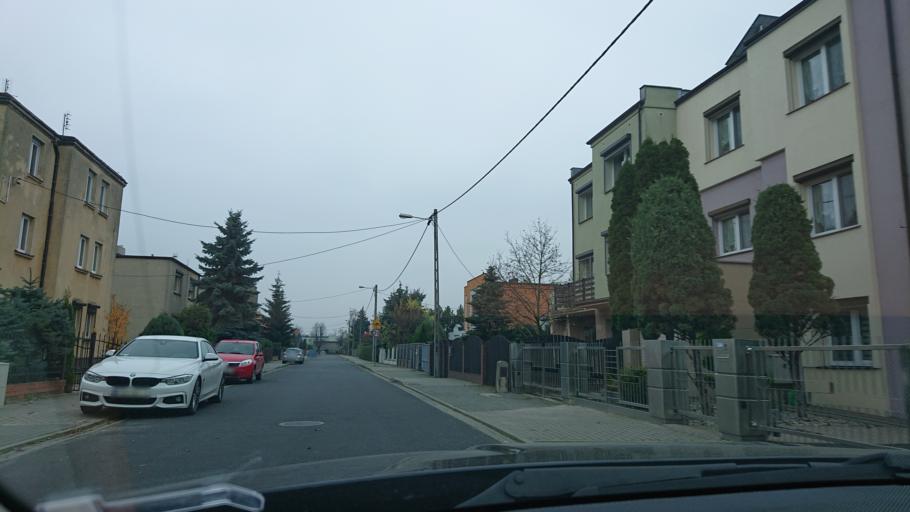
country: PL
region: Greater Poland Voivodeship
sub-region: Powiat gnieznienski
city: Gniezno
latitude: 52.5351
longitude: 17.6240
